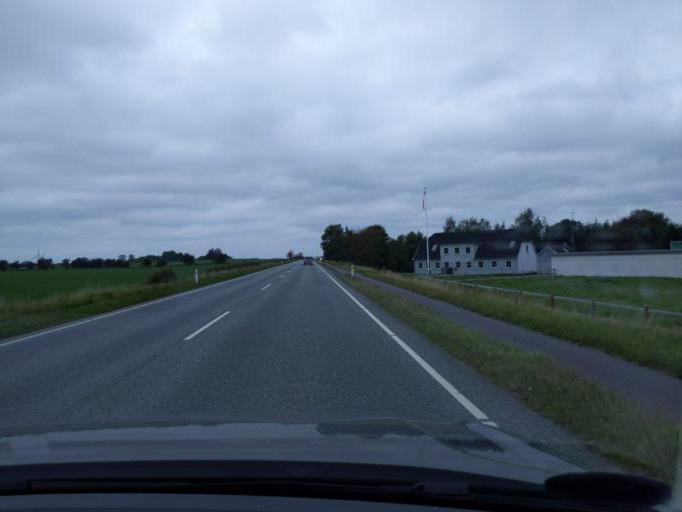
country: DK
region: Central Jutland
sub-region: Randers Kommune
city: Randers
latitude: 56.4979
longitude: 9.9699
